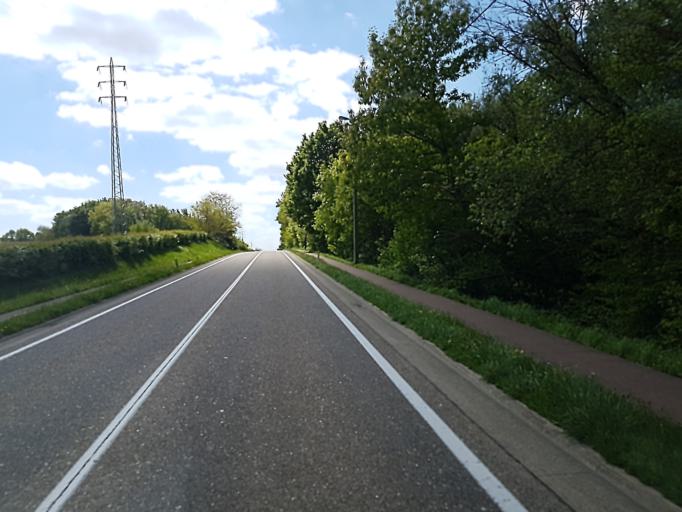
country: BE
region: Flanders
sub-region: Provincie Vlaams-Brabant
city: Bekkevoort
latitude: 50.9122
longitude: 4.9790
